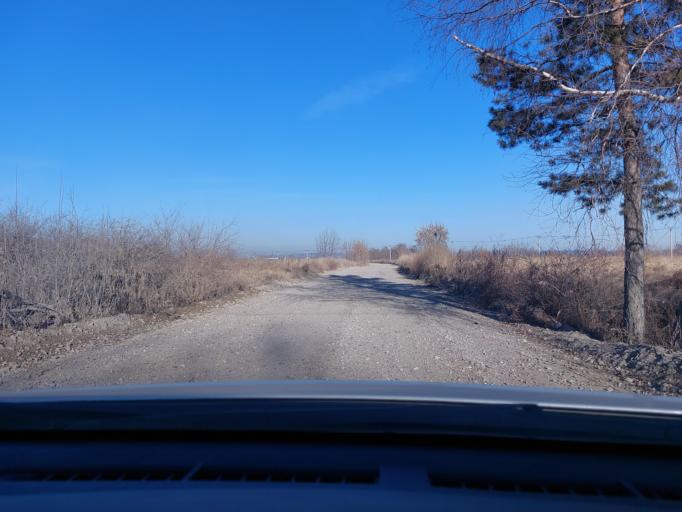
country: RU
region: Irkutsk
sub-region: Irkutskiy Rayon
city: Irkutsk
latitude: 52.3025
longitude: 104.2761
